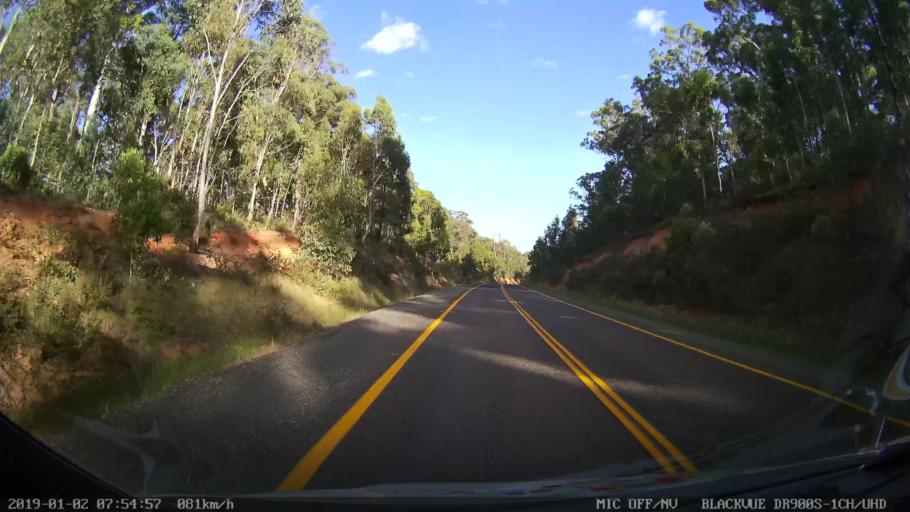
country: AU
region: New South Wales
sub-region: Tumut Shire
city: Tumut
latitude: -35.6906
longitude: 148.4910
